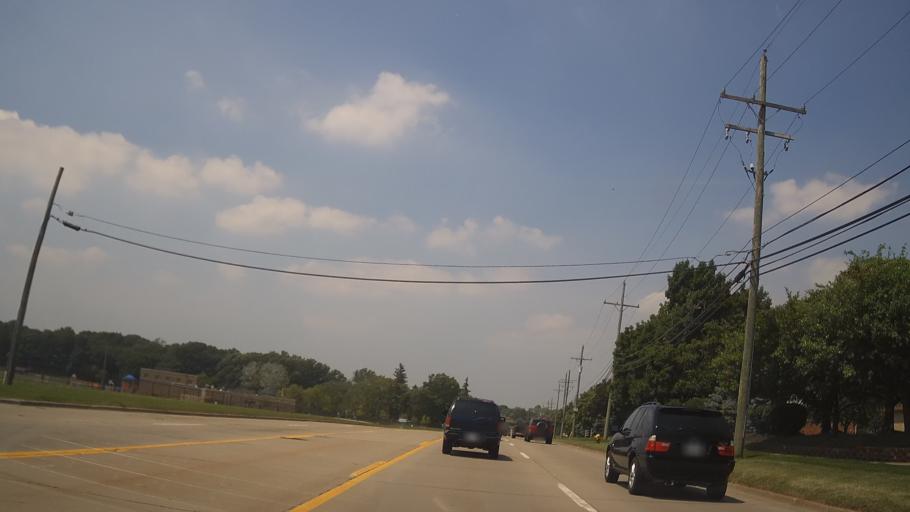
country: US
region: Michigan
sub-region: Macomb County
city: Fraser
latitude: 42.5610
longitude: -82.9653
